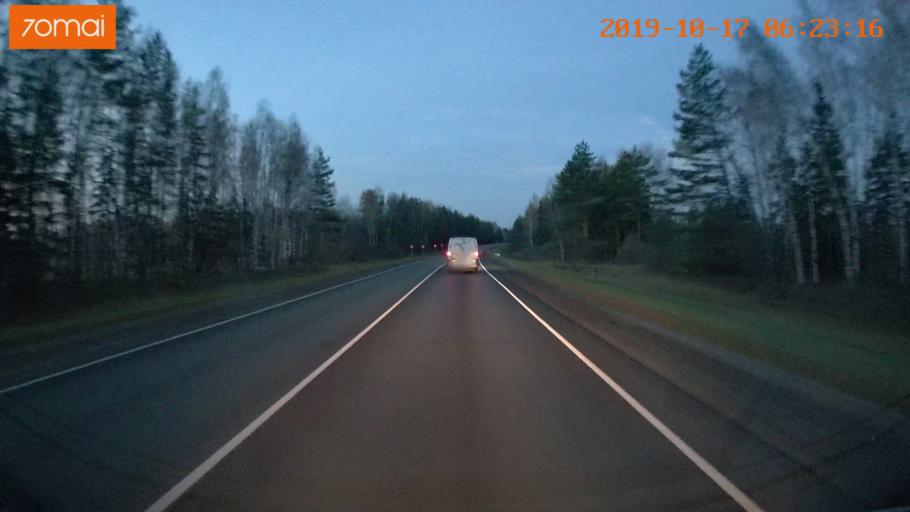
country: RU
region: Ivanovo
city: Lezhnevo
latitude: 56.7846
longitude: 40.8518
